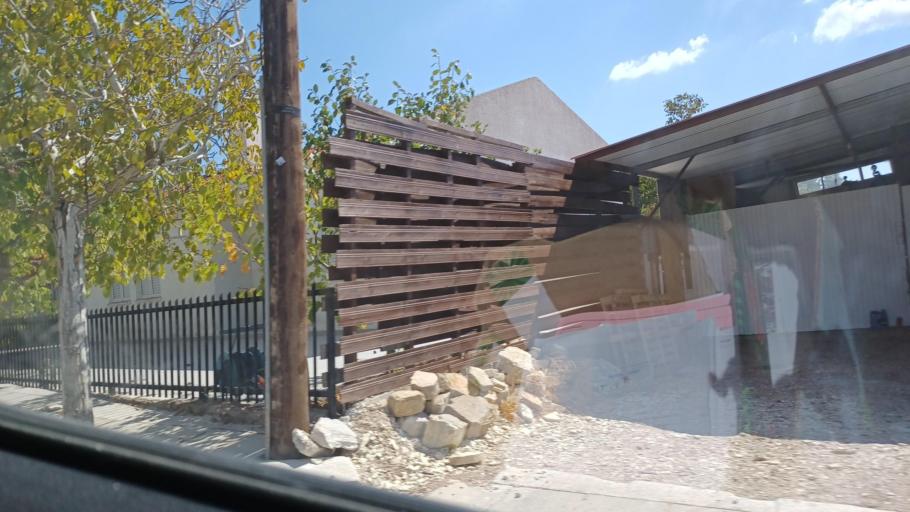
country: CY
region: Pafos
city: Mesogi
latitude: 34.8885
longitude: 32.6207
